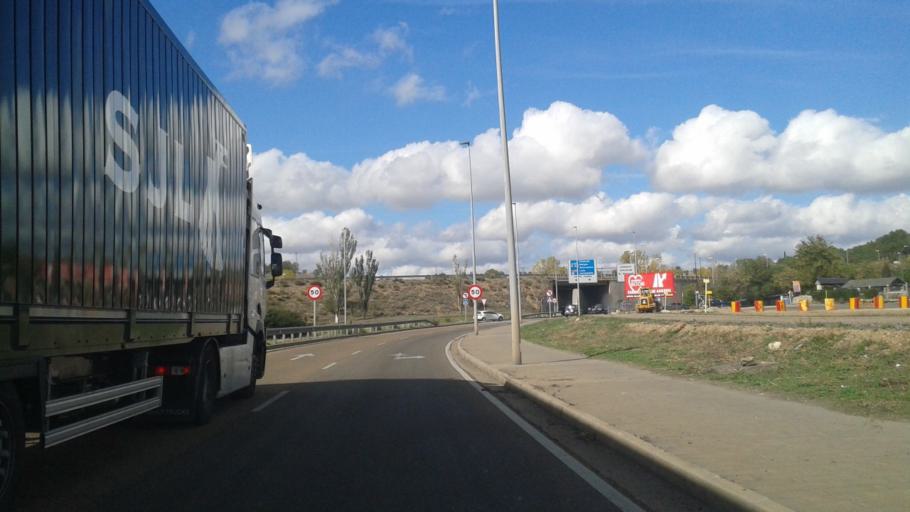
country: ES
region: Castille and Leon
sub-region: Provincia de Valladolid
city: Valladolid
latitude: 41.6770
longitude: -4.7205
